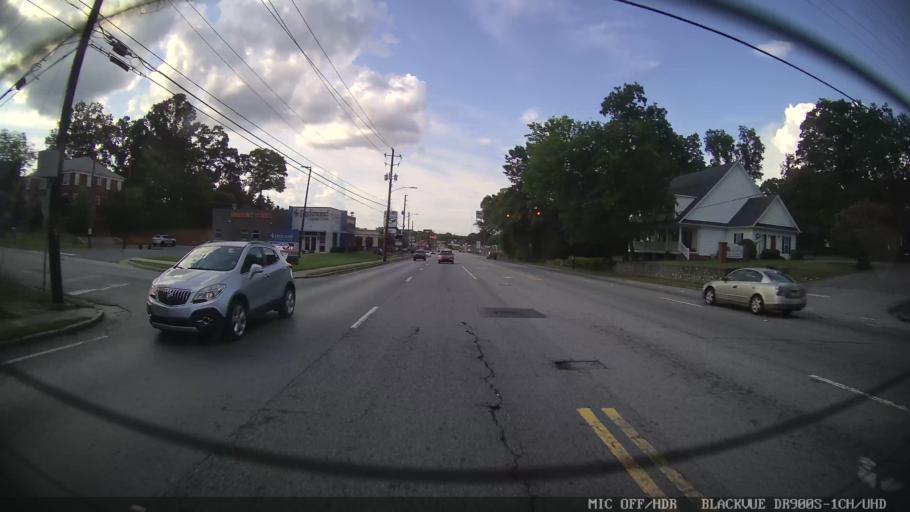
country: US
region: Georgia
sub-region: Floyd County
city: Rome
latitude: 34.2414
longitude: -85.1613
